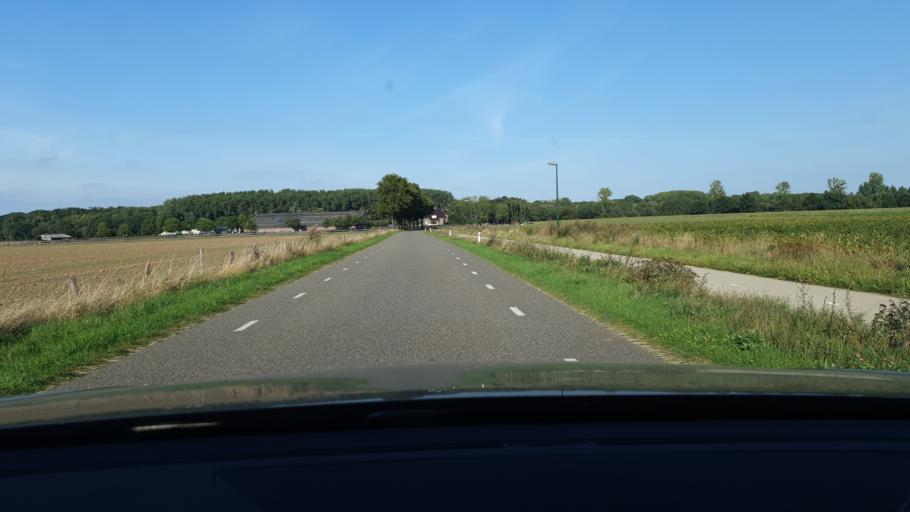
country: NL
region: Limburg
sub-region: Gemeente Sittard-Geleen
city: Born
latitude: 51.0823
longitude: 5.8501
